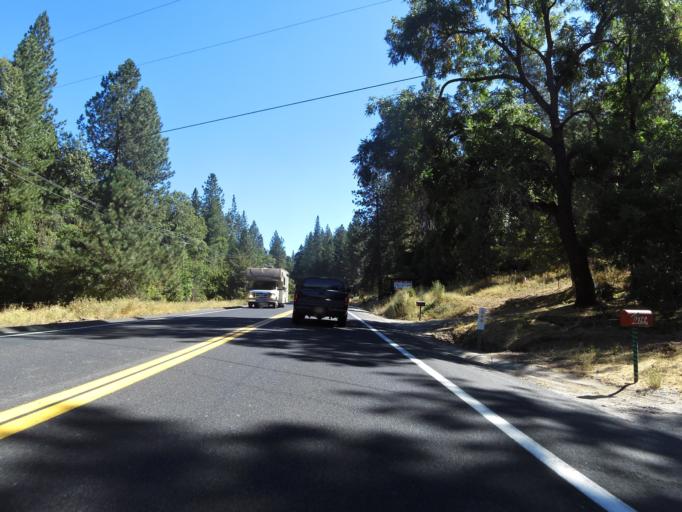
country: US
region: California
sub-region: Calaveras County
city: Forest Meadows
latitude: 38.1663
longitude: -120.4188
